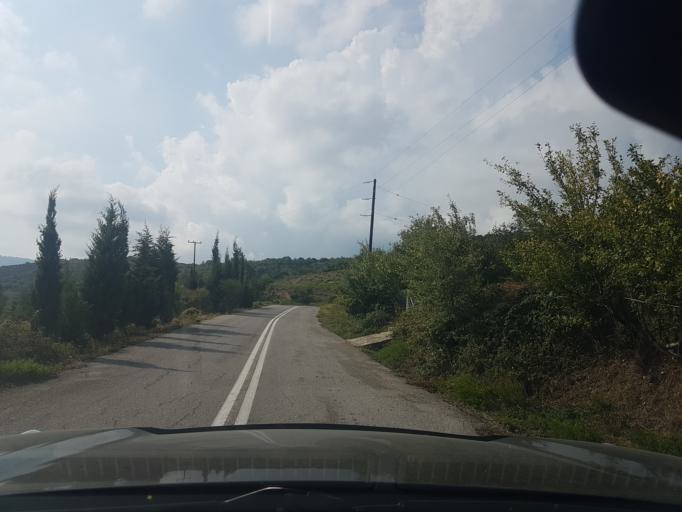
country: GR
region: Central Greece
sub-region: Nomos Evvoias
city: Yimnon
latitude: 38.5398
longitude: 23.9680
